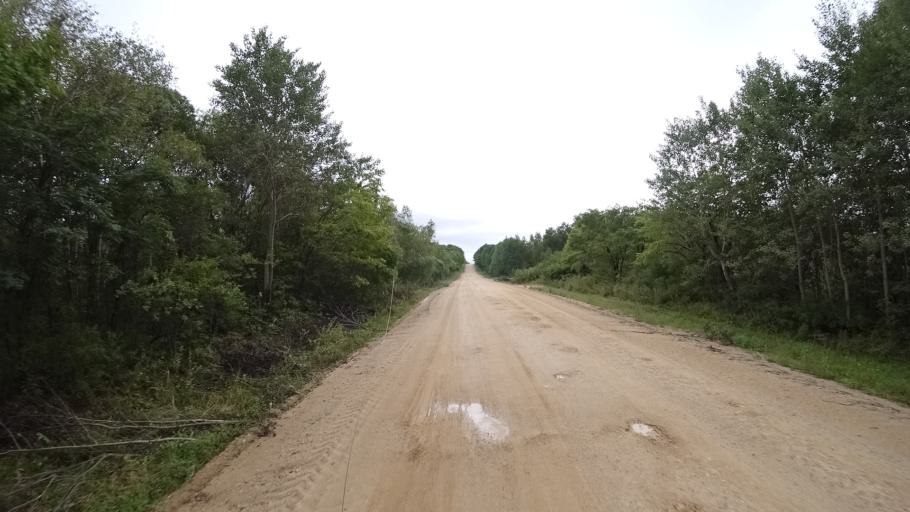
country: RU
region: Primorskiy
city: Monastyrishche
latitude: 44.1126
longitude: 132.6227
